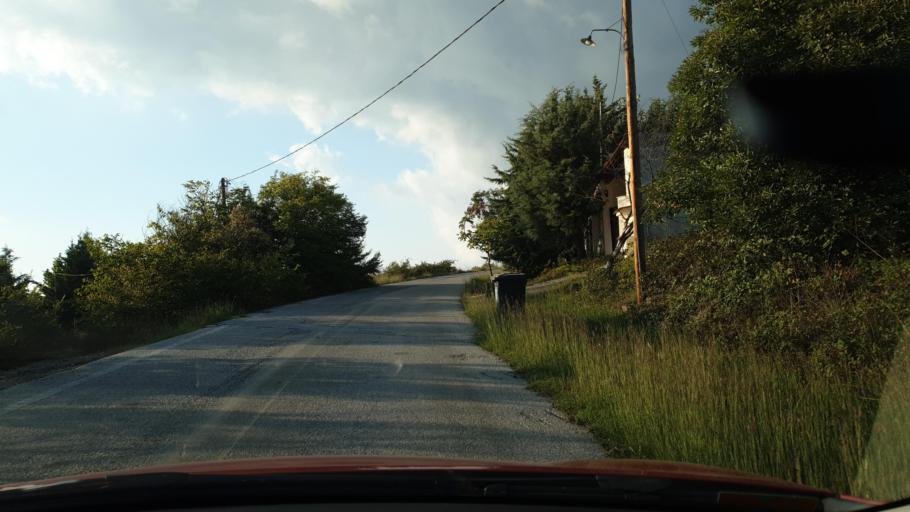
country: GR
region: Central Macedonia
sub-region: Nomos Chalkidikis
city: Galatista
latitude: 40.5255
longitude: 23.2776
